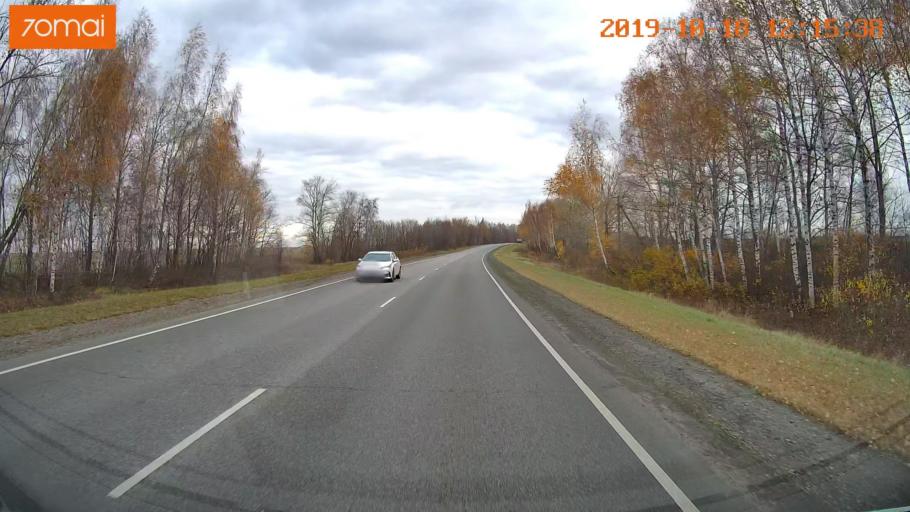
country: RU
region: Rjazan
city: Zakharovo
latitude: 54.4460
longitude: 39.4037
